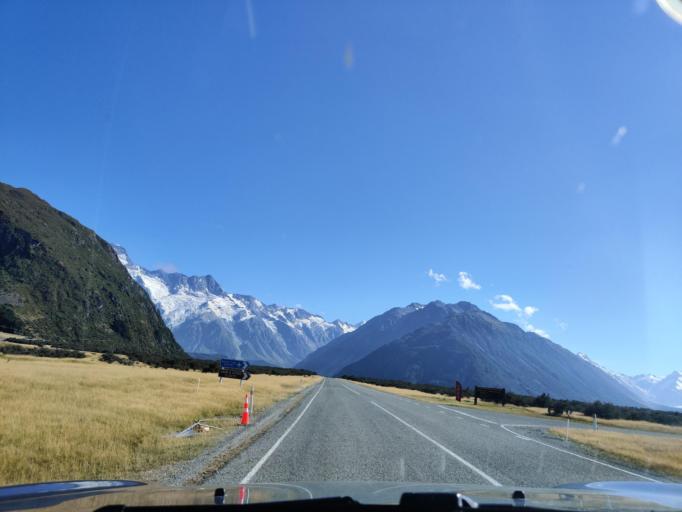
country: NZ
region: Canterbury
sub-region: Timaru District
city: Pleasant Point
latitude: -43.7667
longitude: 170.1232
